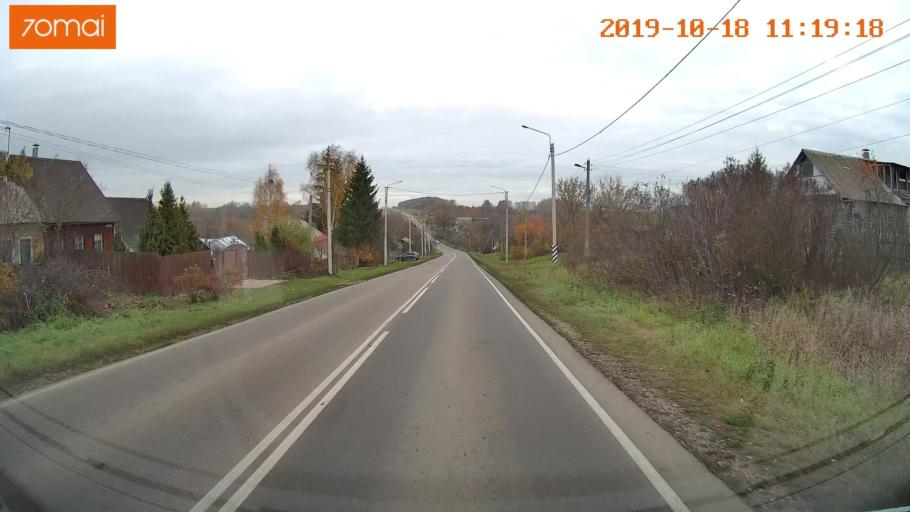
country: RU
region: Tula
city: Kimovsk
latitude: 54.0451
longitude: 38.5531
